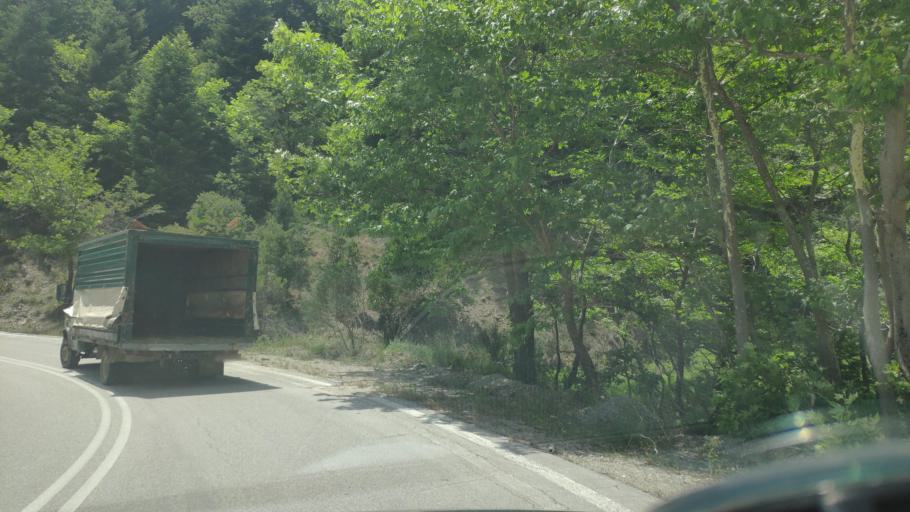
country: GR
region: Thessaly
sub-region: Nomos Kardhitsas
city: Anthiro
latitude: 39.2727
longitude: 21.3491
